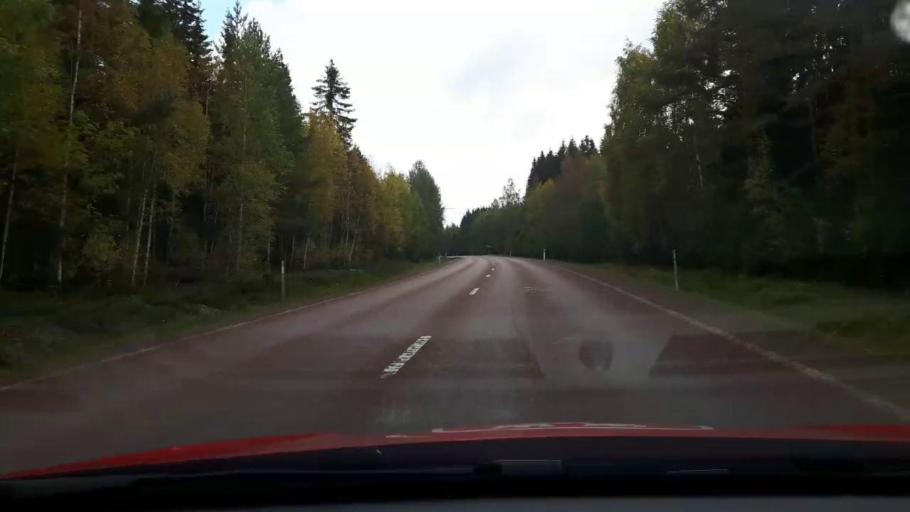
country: SE
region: Gaevleborg
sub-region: Ljusdals Kommun
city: Jaervsoe
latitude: 61.6393
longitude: 16.2378
